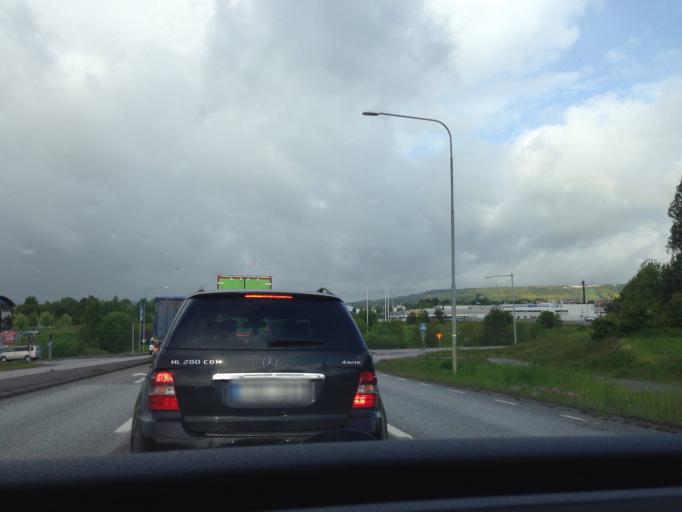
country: SE
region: Vaestra Goetaland
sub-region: Skovde Kommun
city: Skoevde
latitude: 58.3947
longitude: 13.8772
